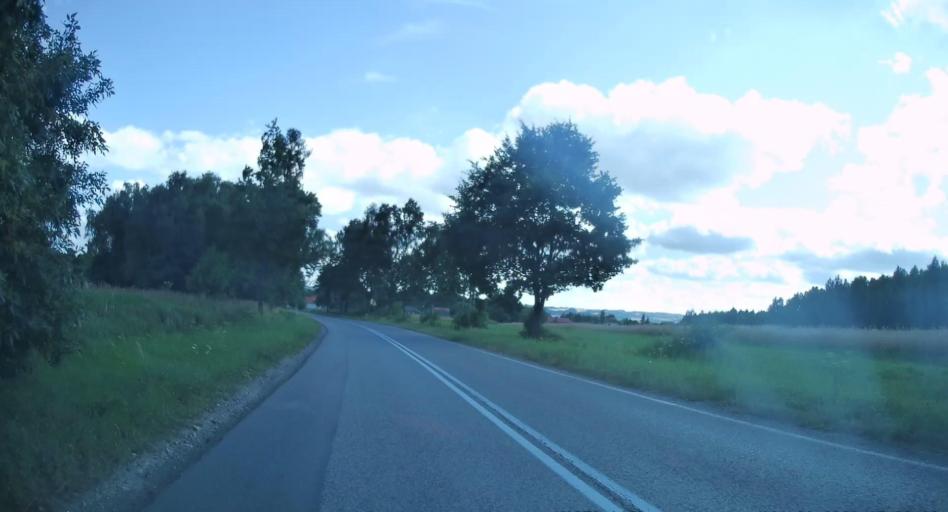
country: PL
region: Swietokrzyskie
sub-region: Powiat kielecki
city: Lagow
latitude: 50.8048
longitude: 21.0796
